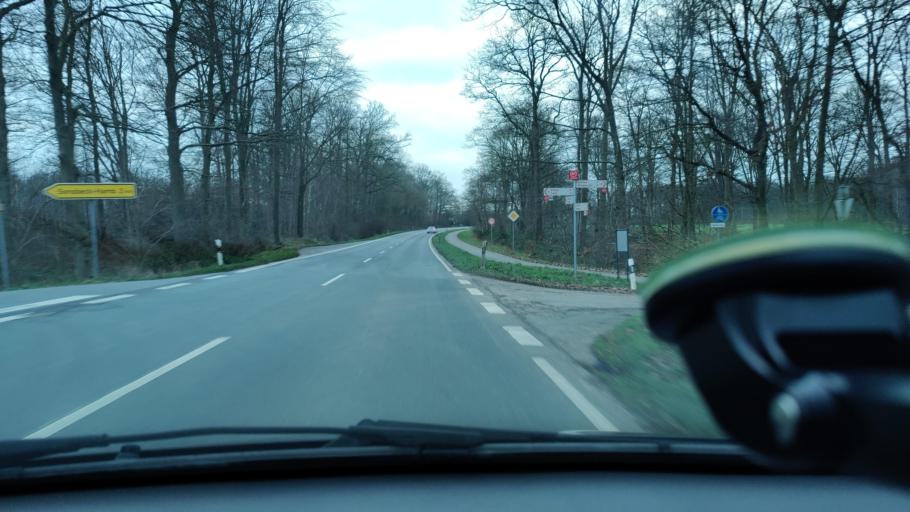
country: DE
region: North Rhine-Westphalia
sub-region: Regierungsbezirk Dusseldorf
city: Sonsbeck
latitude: 51.5849
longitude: 6.3857
